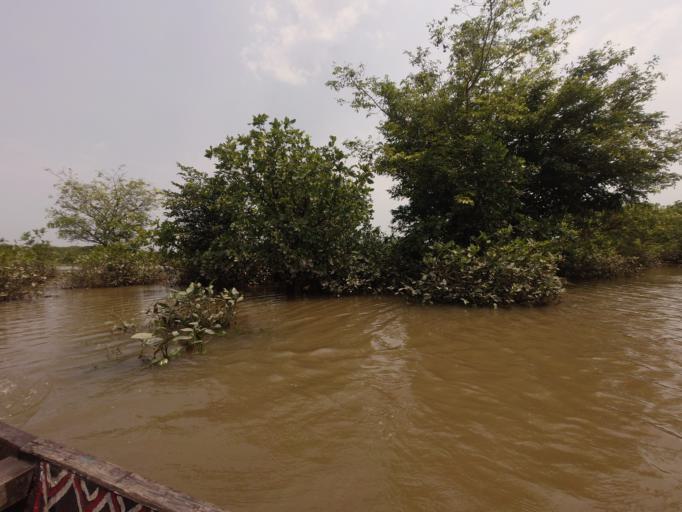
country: BD
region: Sylhet
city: Sylhet
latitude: 25.0139
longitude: 91.9220
